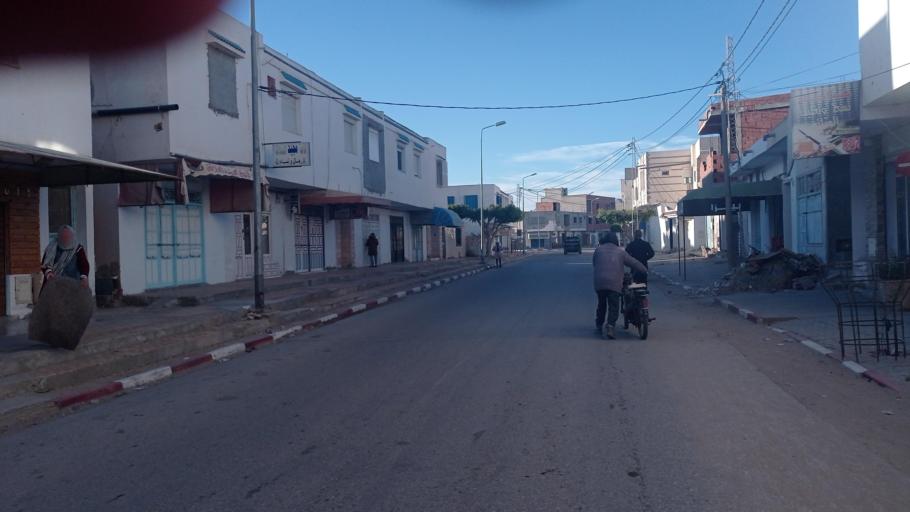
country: TN
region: Qabis
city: Gabes
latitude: 33.8419
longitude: 10.1180
